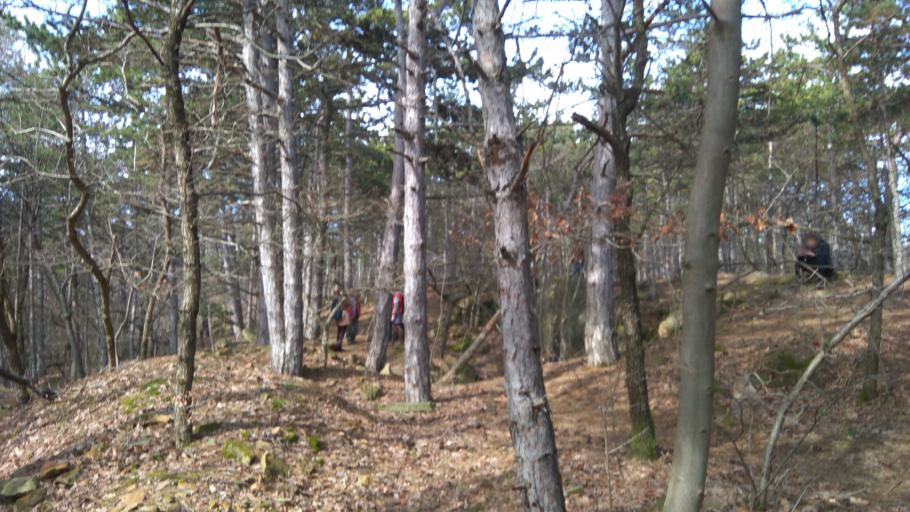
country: HU
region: Pest
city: Pilisborosjeno
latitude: 47.6182
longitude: 19.0117
